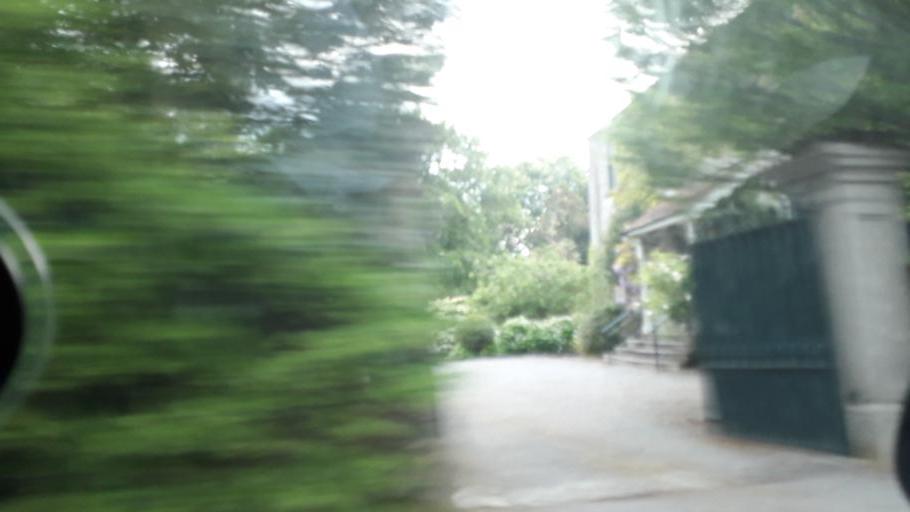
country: IE
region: Leinster
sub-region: Kildare
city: Celbridge
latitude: 53.3303
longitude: -6.5487
